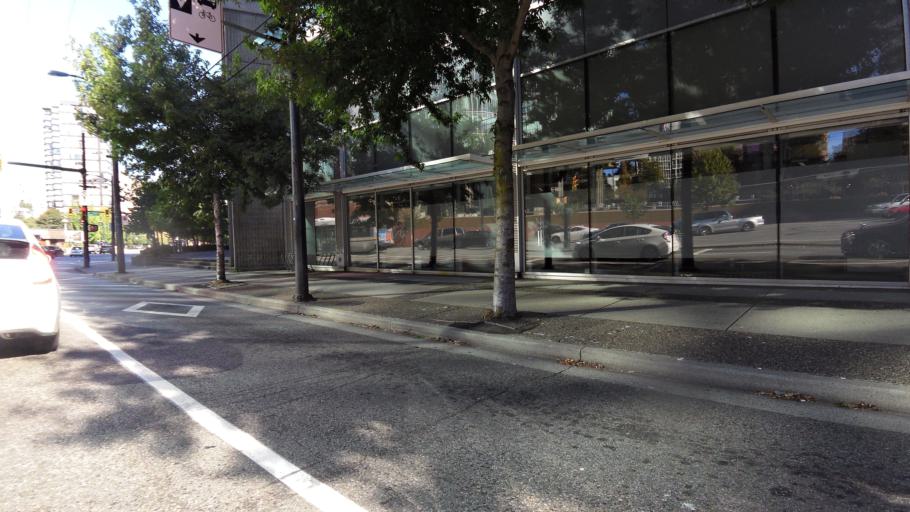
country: CA
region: British Columbia
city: West End
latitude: 49.2904
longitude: -123.1298
